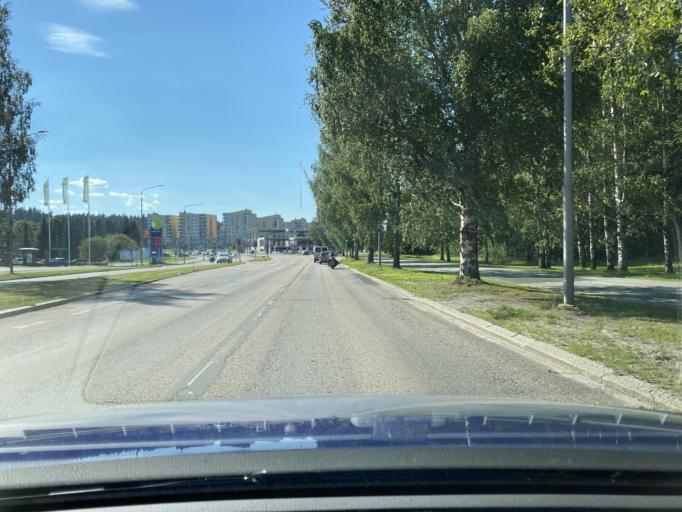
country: FI
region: Pirkanmaa
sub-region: Tampere
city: Tampere
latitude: 61.4936
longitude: 23.8259
